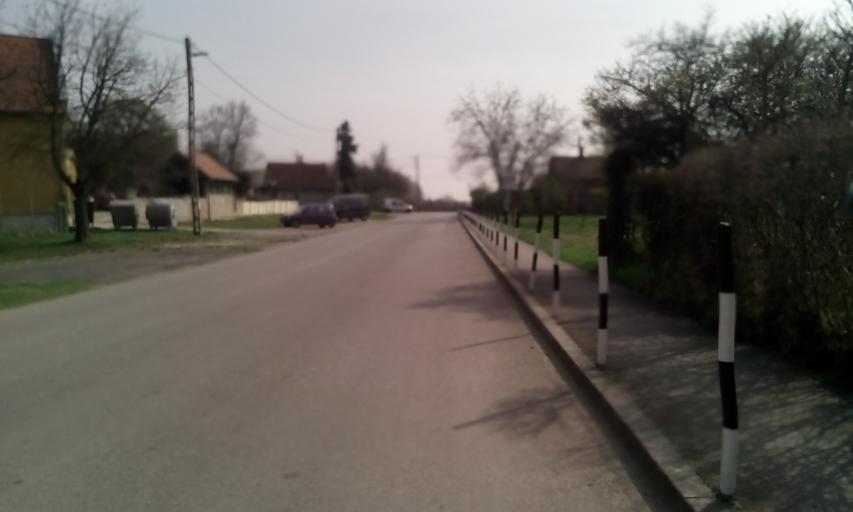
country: HU
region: Tolna
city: Decs
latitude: 46.2836
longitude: 18.7564
